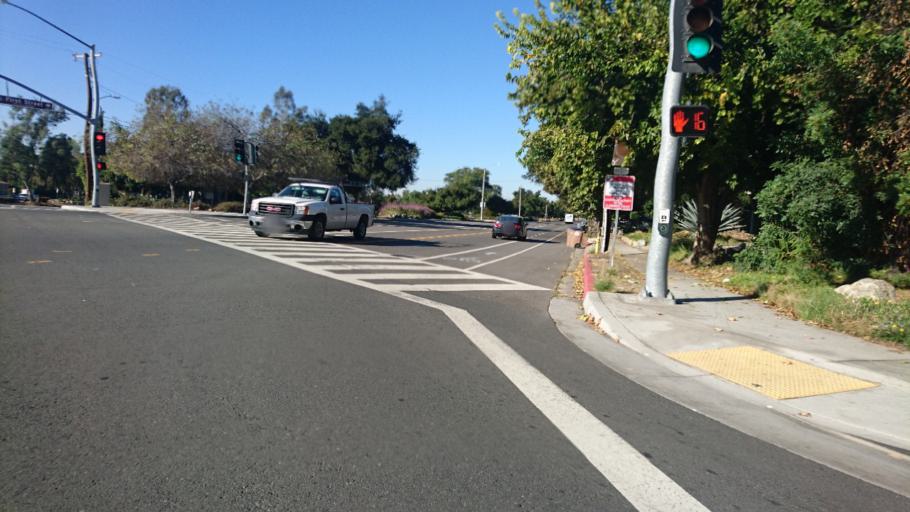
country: US
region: California
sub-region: Los Angeles County
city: Claremont
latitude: 34.0954
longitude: -117.7047
